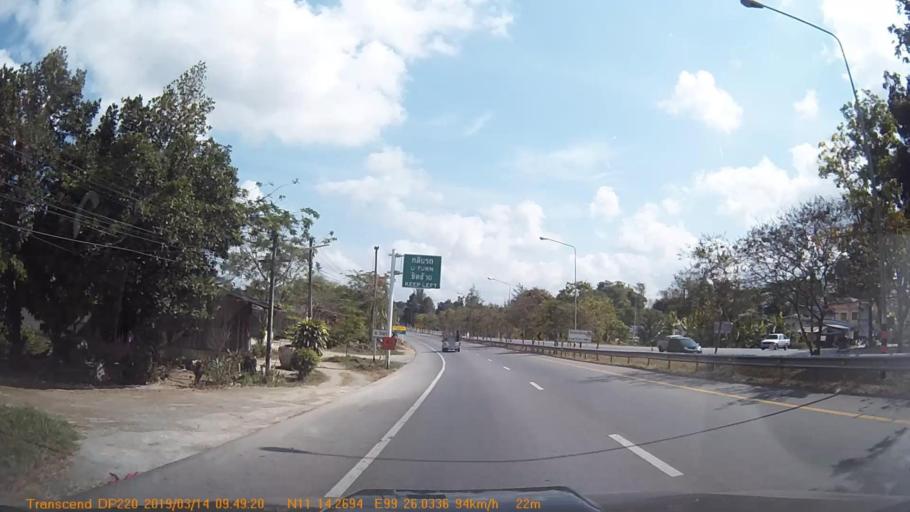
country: TH
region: Prachuap Khiri Khan
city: Bang Saphan
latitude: 11.2382
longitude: 99.4342
